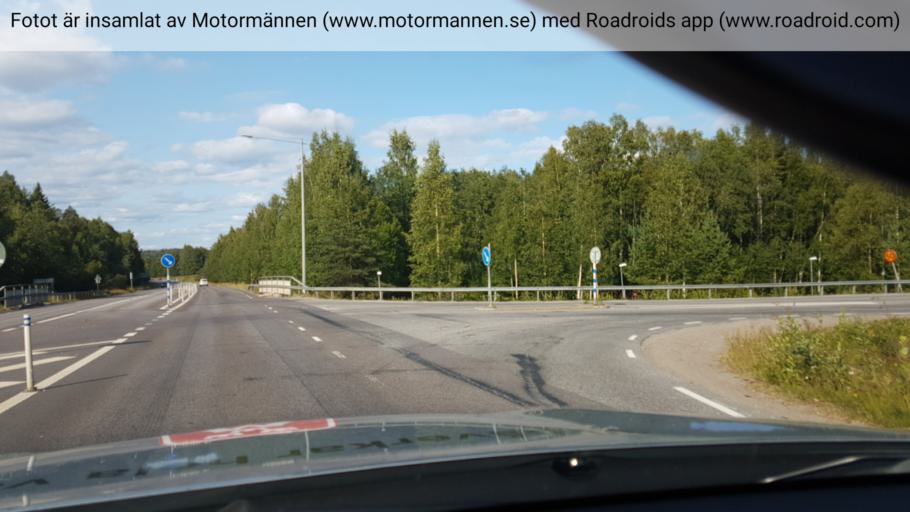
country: SE
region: Norrbotten
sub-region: Pitea Kommun
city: Pitea
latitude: 65.2979
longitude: 21.5104
